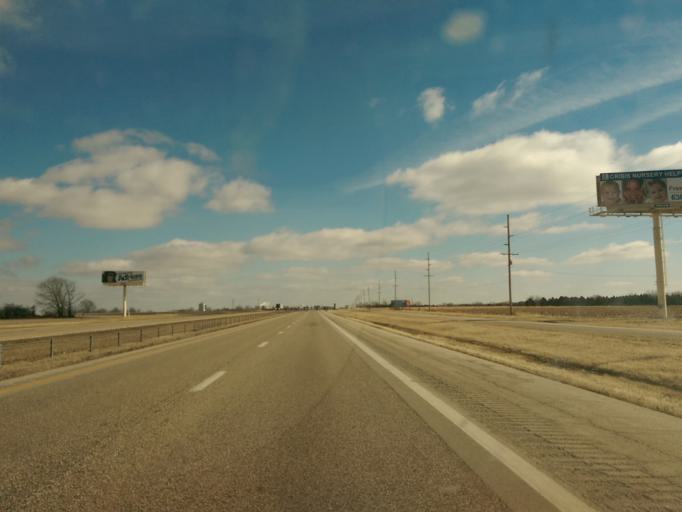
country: US
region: Missouri
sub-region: Montgomery County
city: Montgomery City
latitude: 38.8858
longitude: -91.4080
